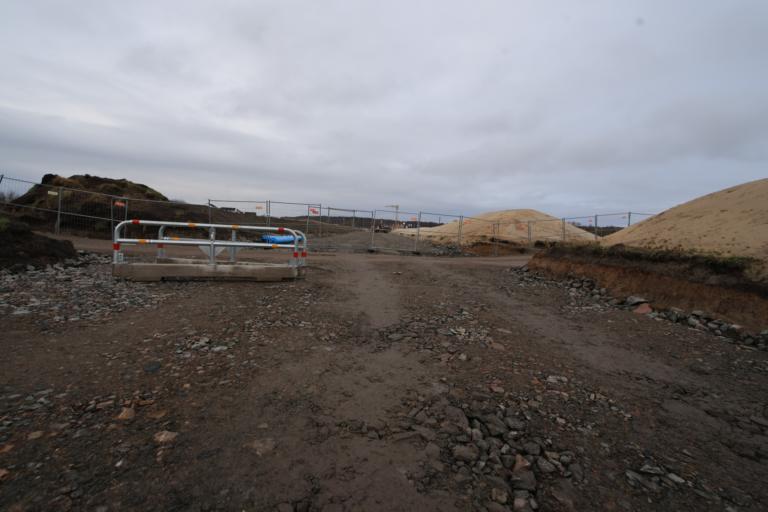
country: SE
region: Halland
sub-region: Varbergs Kommun
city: Traslovslage
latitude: 57.0861
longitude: 12.2907
